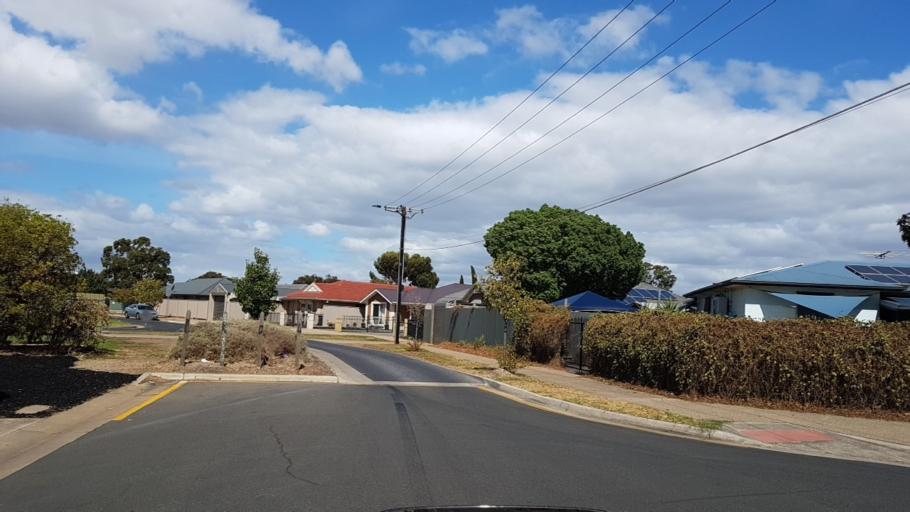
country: AU
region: South Australia
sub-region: Charles Sturt
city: Woodville North
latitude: -34.8561
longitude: 138.5430
